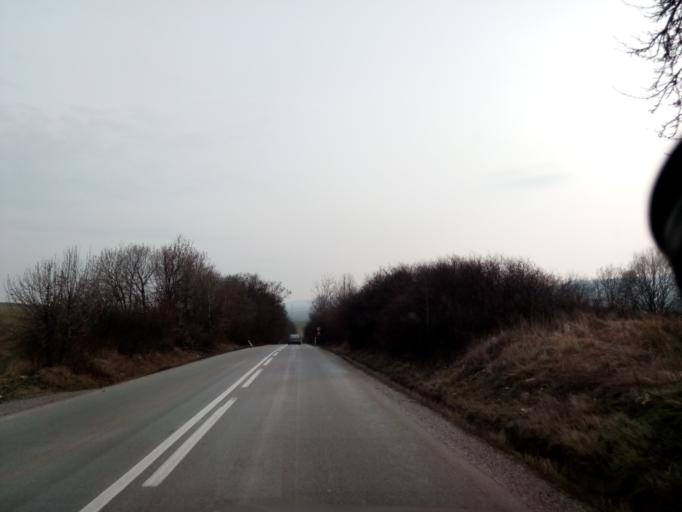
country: SK
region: Kosicky
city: Secovce
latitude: 48.6314
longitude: 21.5544
